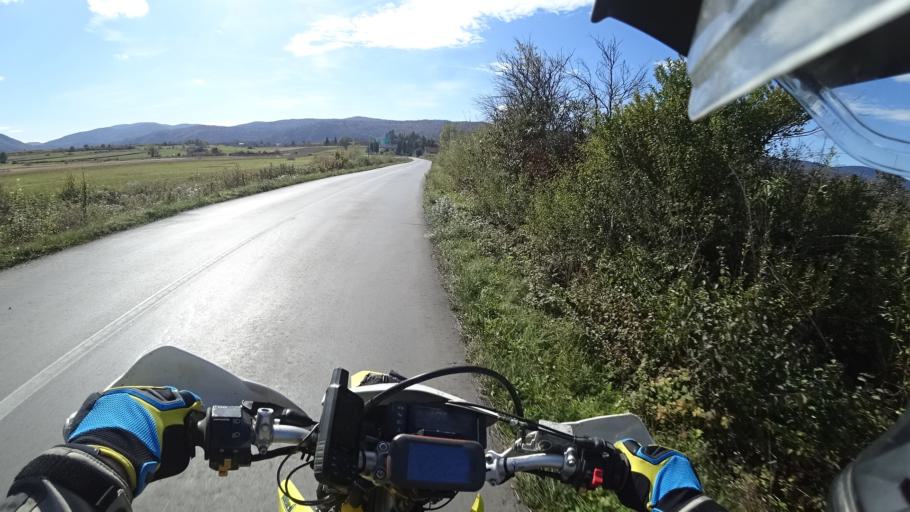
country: HR
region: Karlovacka
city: Plaski
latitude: 45.0976
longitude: 15.3536
